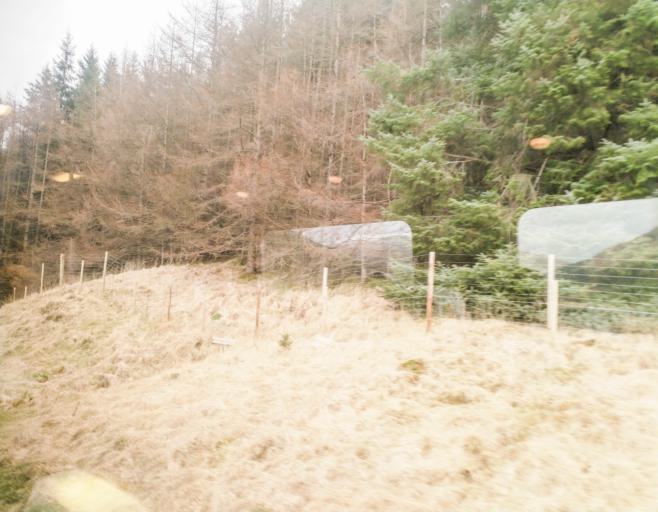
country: GB
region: Scotland
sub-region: Argyll and Bute
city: Garelochhead
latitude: 56.4387
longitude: -4.7066
